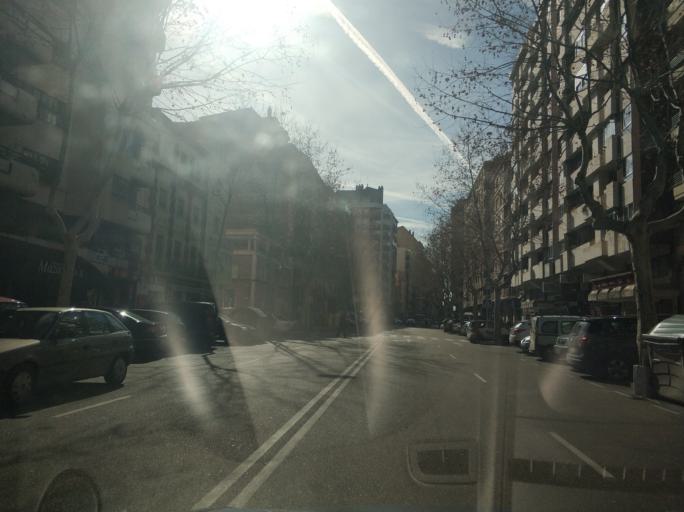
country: ES
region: Castille and Leon
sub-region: Provincia de Zamora
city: Zamora
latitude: 41.5107
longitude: -5.7414
